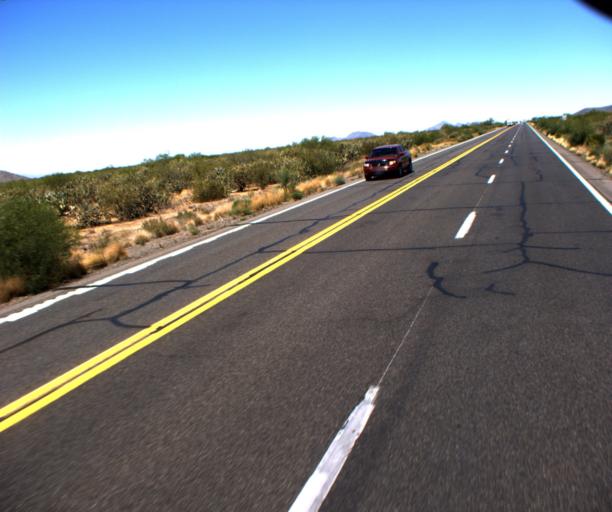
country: US
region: Arizona
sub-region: Yavapai County
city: Congress
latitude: 34.1274
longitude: -112.9562
